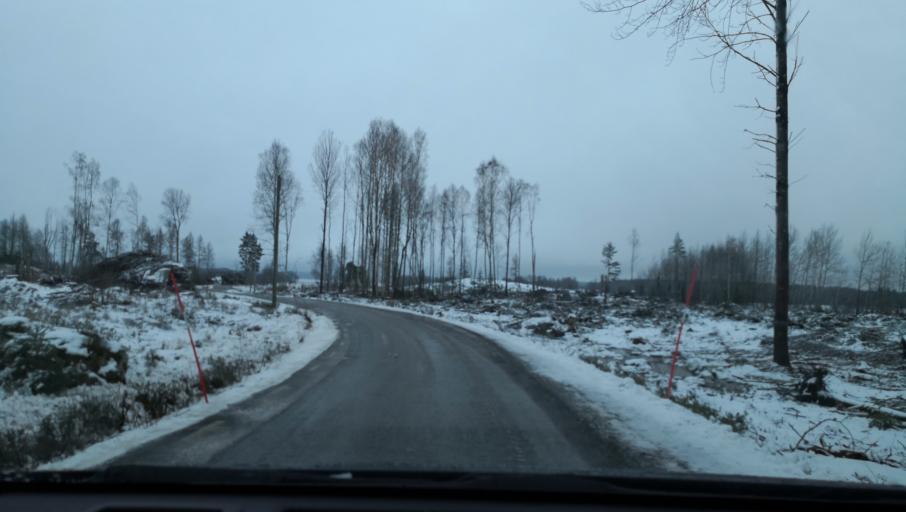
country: SE
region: Vaestmanland
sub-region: Kopings Kommun
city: Kolsva
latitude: 59.5453
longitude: 15.8806
